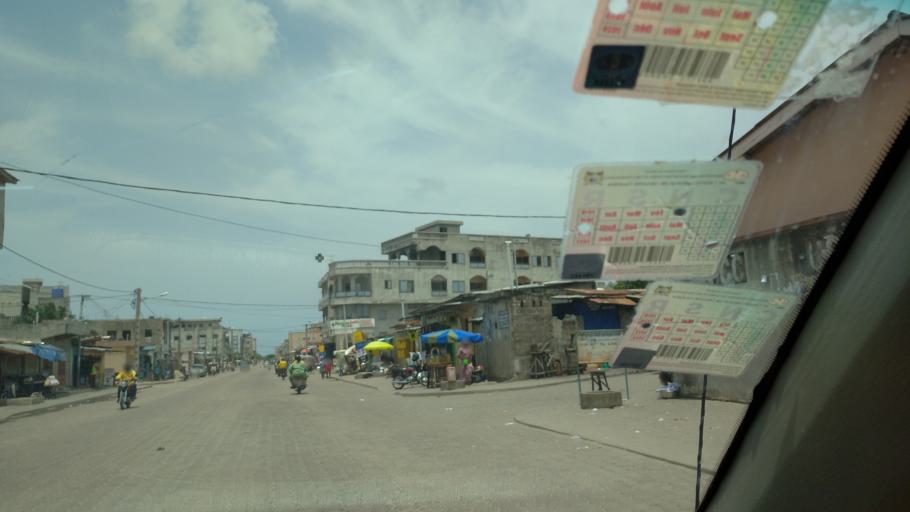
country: BJ
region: Littoral
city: Cotonou
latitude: 6.3918
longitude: 2.4532
